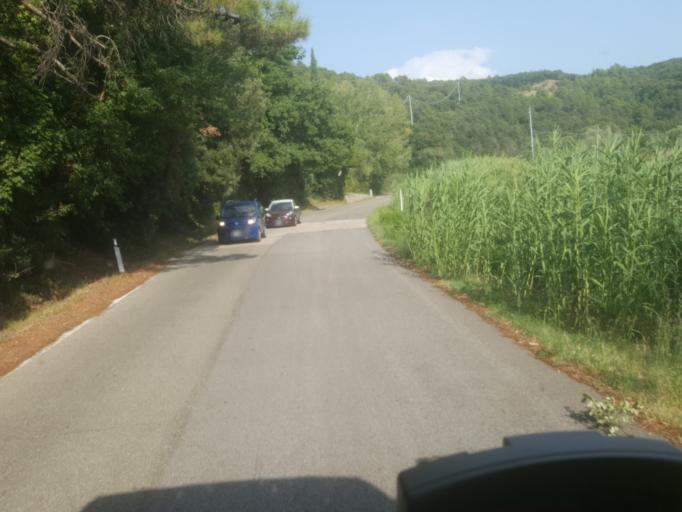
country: IT
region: Tuscany
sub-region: Province of Florence
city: Montaione
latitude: 43.4879
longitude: 10.9063
